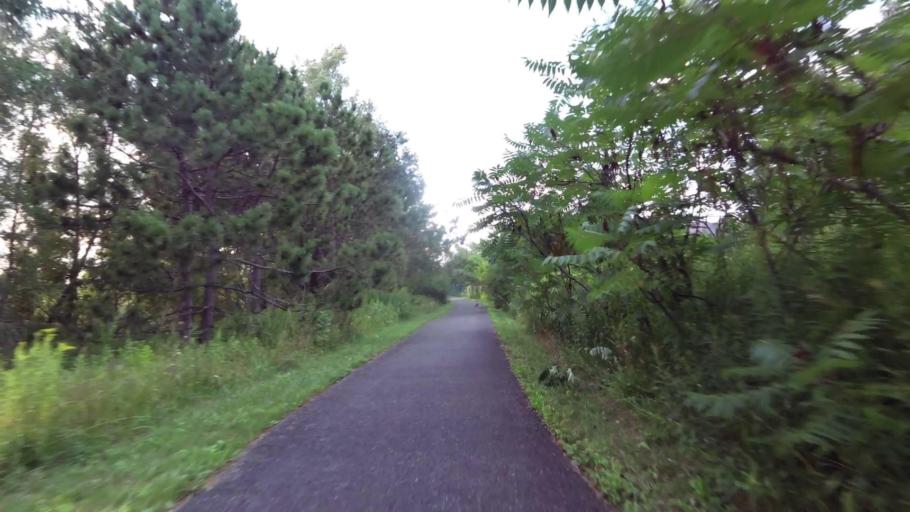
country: CA
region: Ontario
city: Ottawa
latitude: 45.2691
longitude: -75.5787
